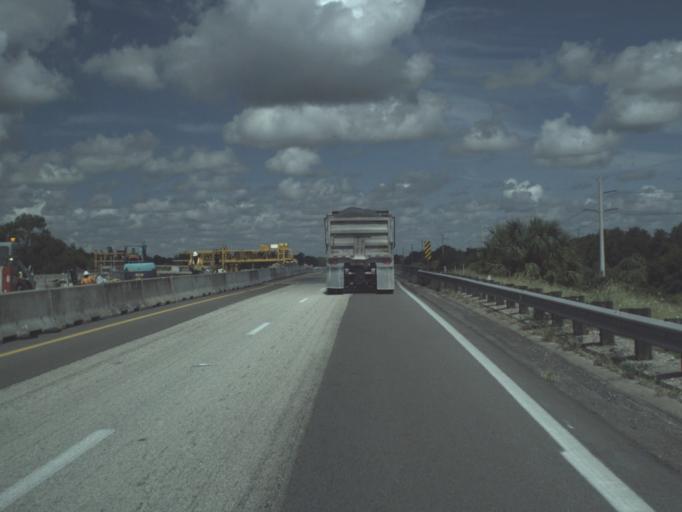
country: US
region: Florida
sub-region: Charlotte County
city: Port Charlotte
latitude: 27.0595
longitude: -82.0842
